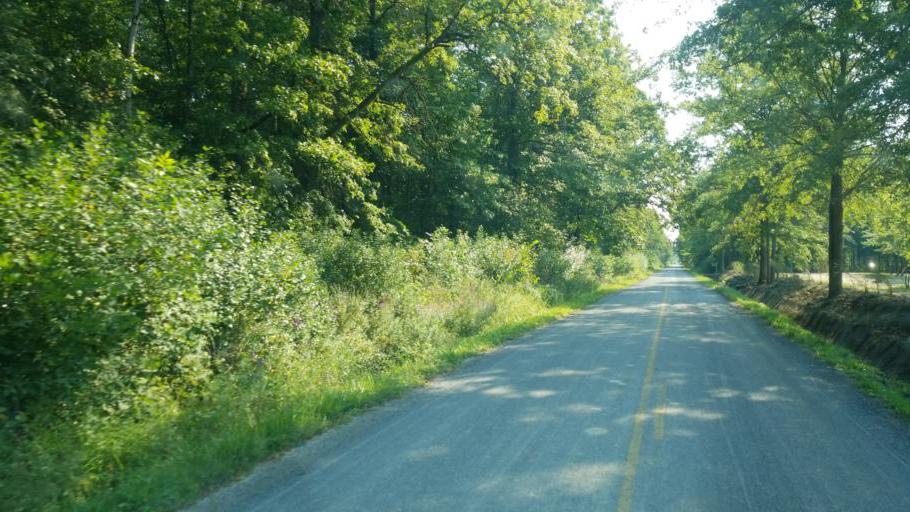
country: US
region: Ohio
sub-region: Ashtabula County
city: Orwell
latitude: 41.4756
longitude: -80.9134
